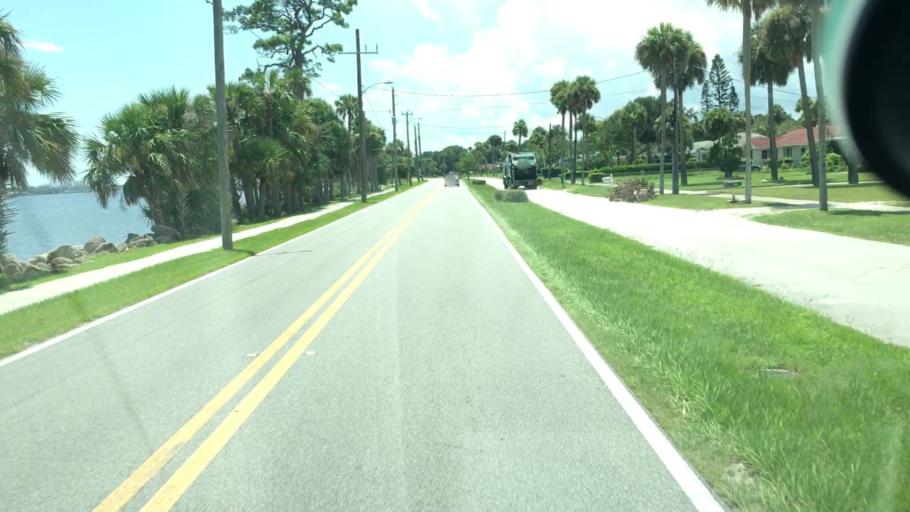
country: US
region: Florida
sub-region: Volusia County
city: Ormond Beach
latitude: 29.2677
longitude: -81.0466
